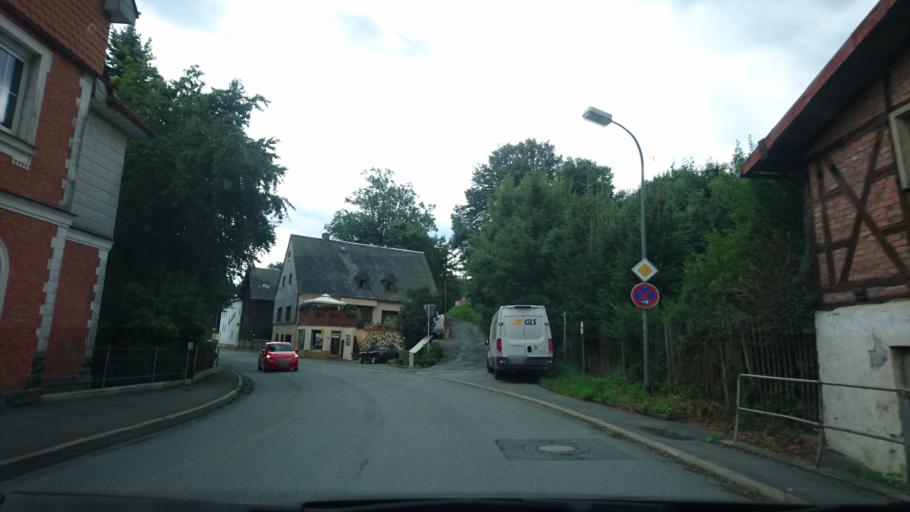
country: DE
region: Bavaria
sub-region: Upper Franconia
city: Lichtenberg
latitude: 50.3818
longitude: 11.6749
